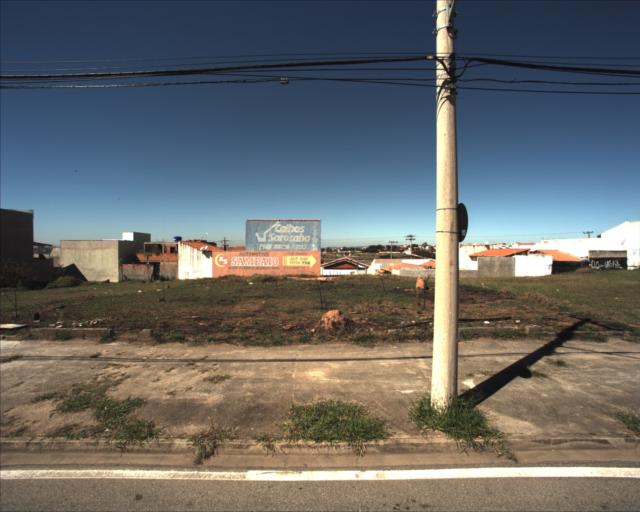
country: BR
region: Sao Paulo
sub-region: Sorocaba
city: Sorocaba
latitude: -23.4851
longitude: -47.5105
